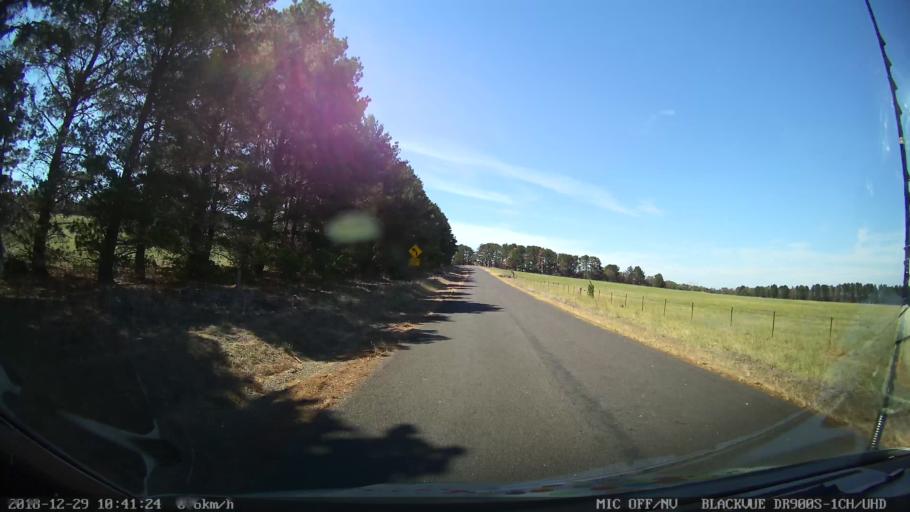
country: AU
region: New South Wales
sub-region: Palerang
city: Bungendore
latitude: -35.0248
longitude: 149.5211
